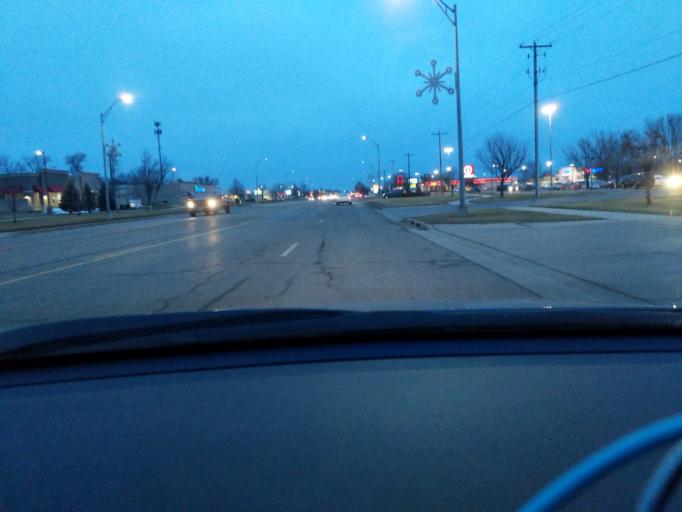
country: US
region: Minnesota
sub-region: Kandiyohi County
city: Willmar
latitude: 45.0971
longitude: -95.0425
